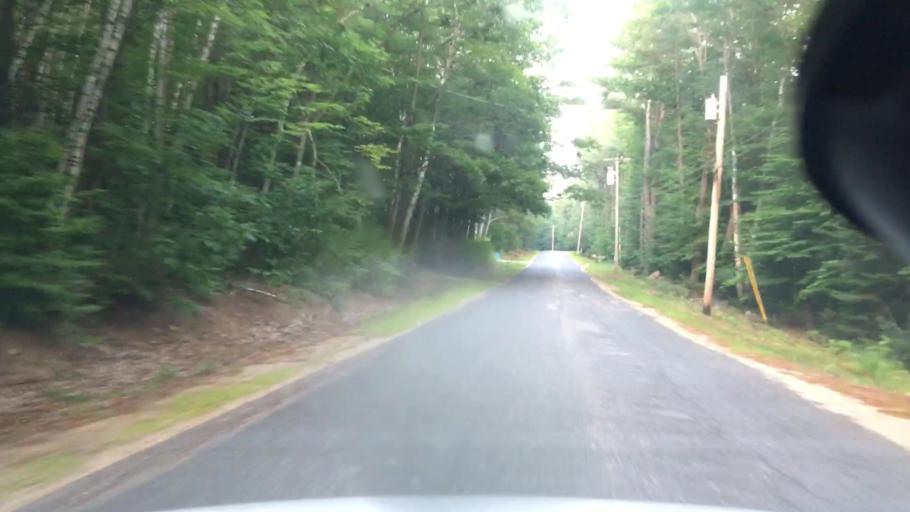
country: US
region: Maine
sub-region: Oxford County
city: Bethel
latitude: 44.4080
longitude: -70.8774
